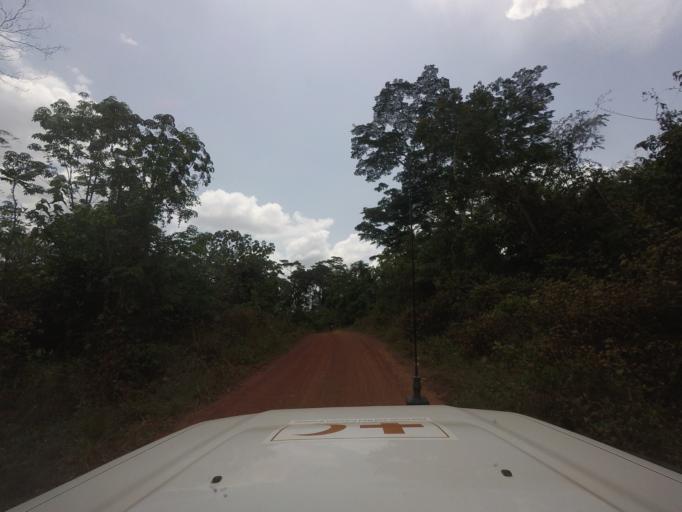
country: LR
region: Bong
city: Gbarnga
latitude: 7.1444
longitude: -9.2209
